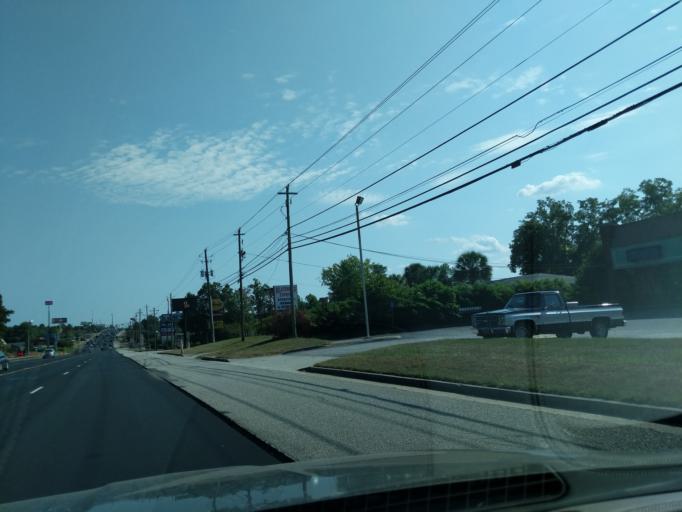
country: US
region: Georgia
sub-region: Columbia County
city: Evans
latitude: 33.4894
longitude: -82.1356
